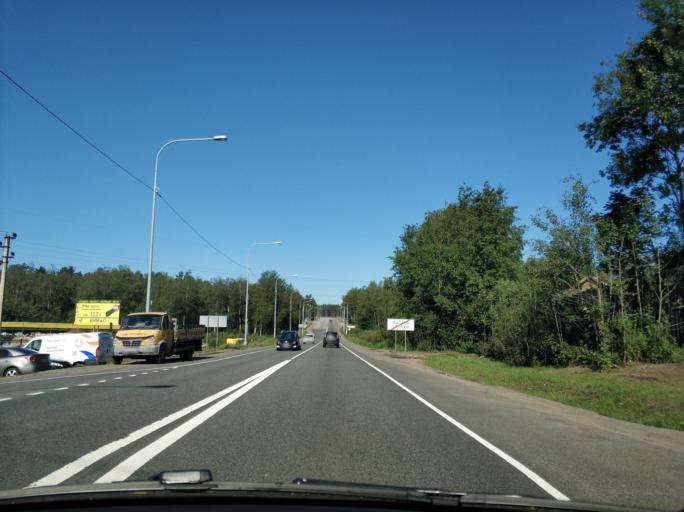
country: RU
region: Leningrad
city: Sapernoye
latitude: 60.6824
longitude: 29.9973
